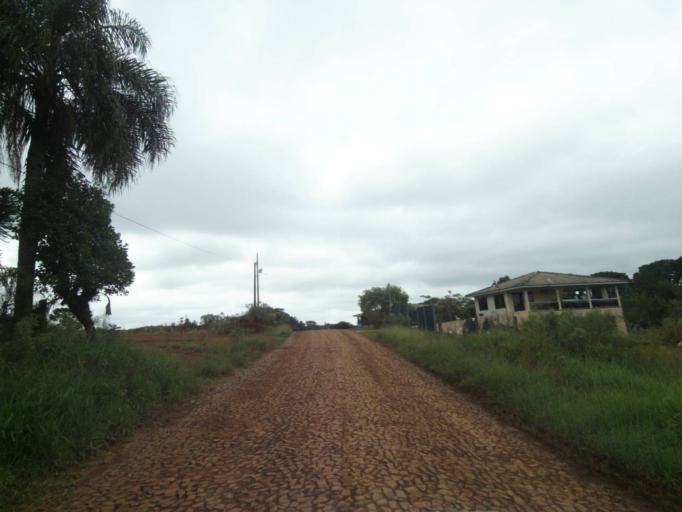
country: BR
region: Parana
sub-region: Pitanga
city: Pitanga
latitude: -24.9364
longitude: -51.8671
